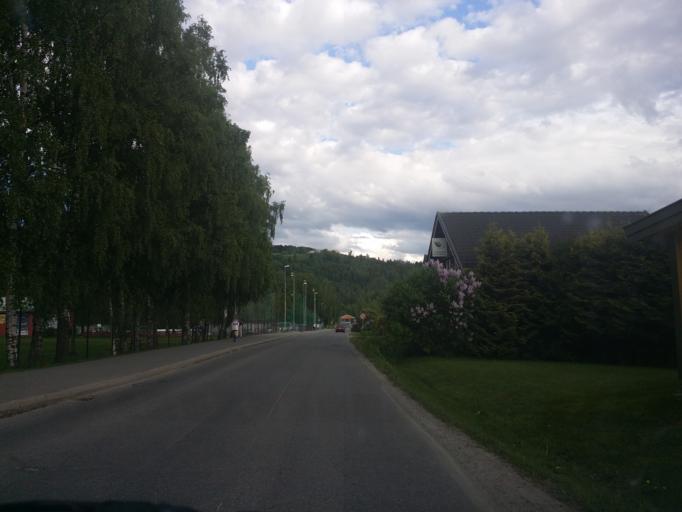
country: NO
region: Hedmark
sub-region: Ringsaker
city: Brumunddal
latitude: 60.8918
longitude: 10.9449
